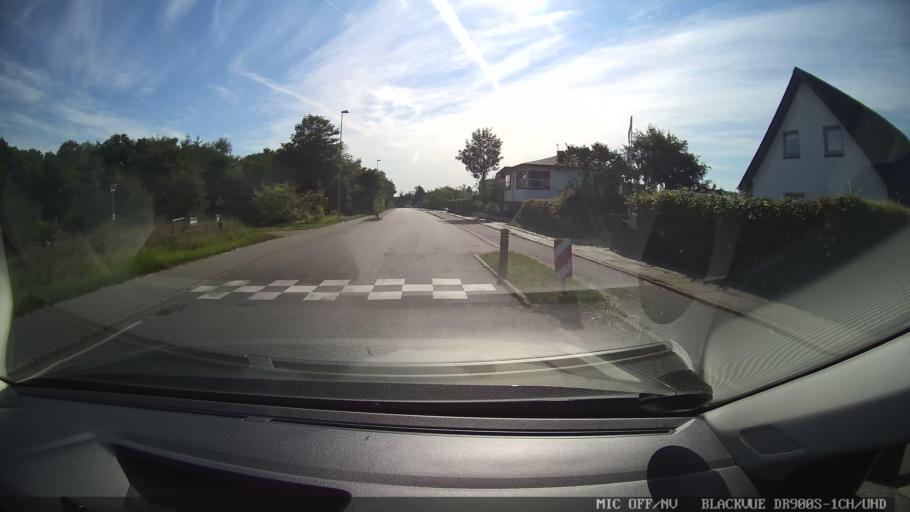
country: DK
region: North Denmark
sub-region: Mariagerfjord Kommune
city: Arden
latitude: 56.7654
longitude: 9.8680
